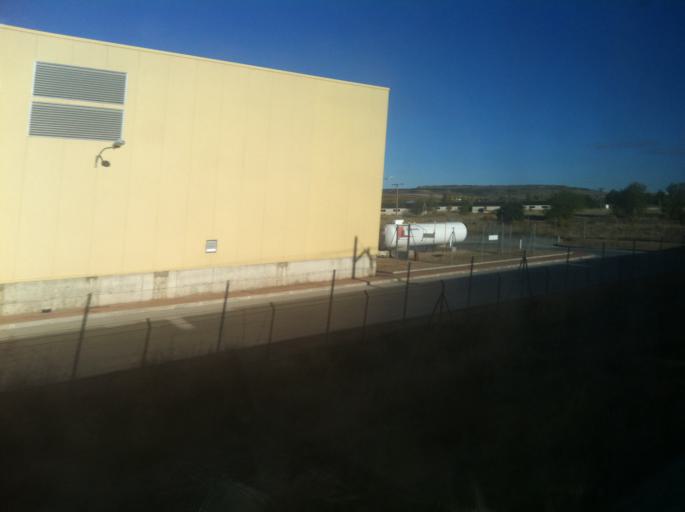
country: ES
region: Castille and Leon
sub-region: Provincia de Valladolid
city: Cubillas de Santa Marta
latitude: 41.8232
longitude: -4.5707
